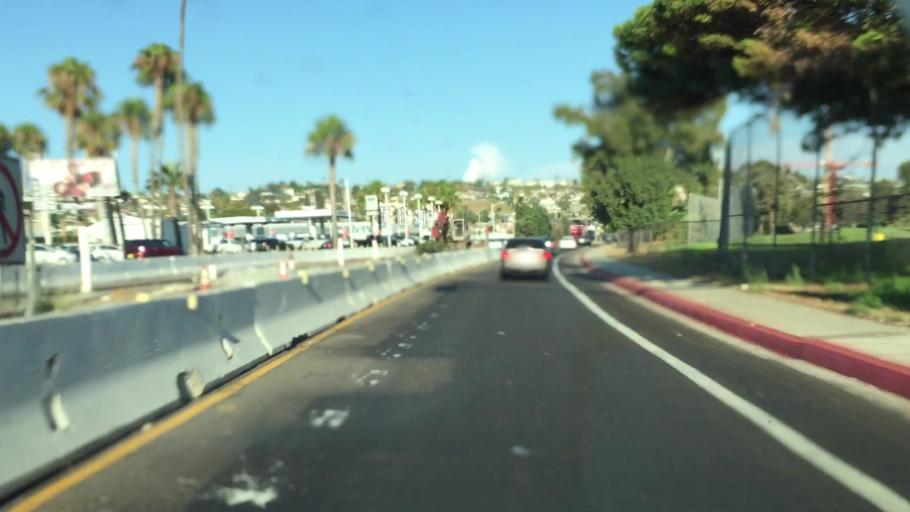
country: US
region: California
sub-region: San Diego County
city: La Jolla
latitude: 32.8023
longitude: -117.2177
